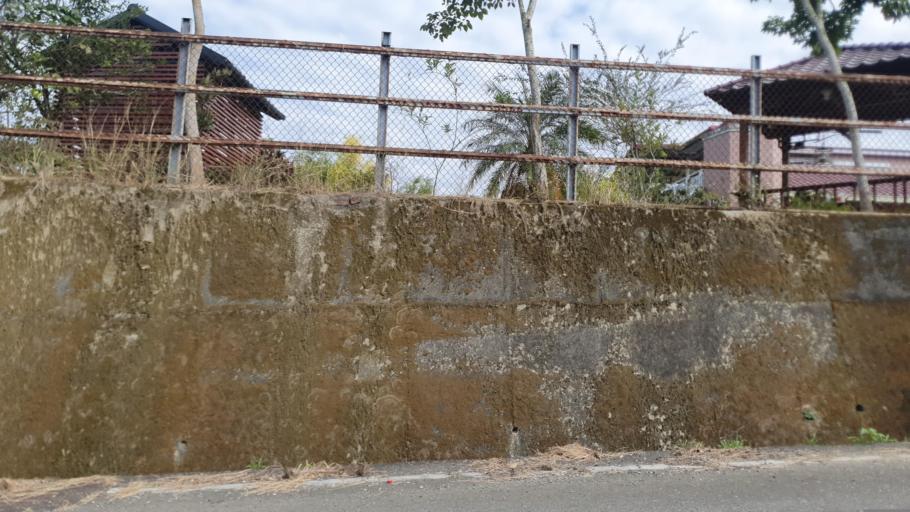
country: TW
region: Taiwan
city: Yujing
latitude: 23.0126
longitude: 120.4171
